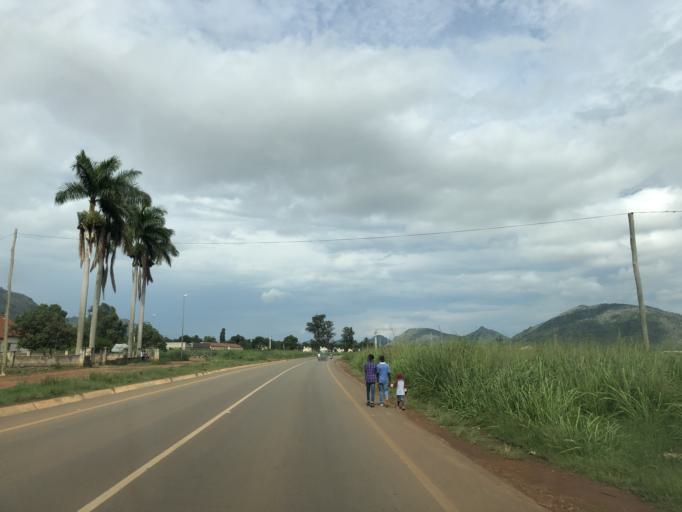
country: AO
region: Cuanza Sul
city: Uacu Cungo
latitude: -11.3517
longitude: 15.1130
